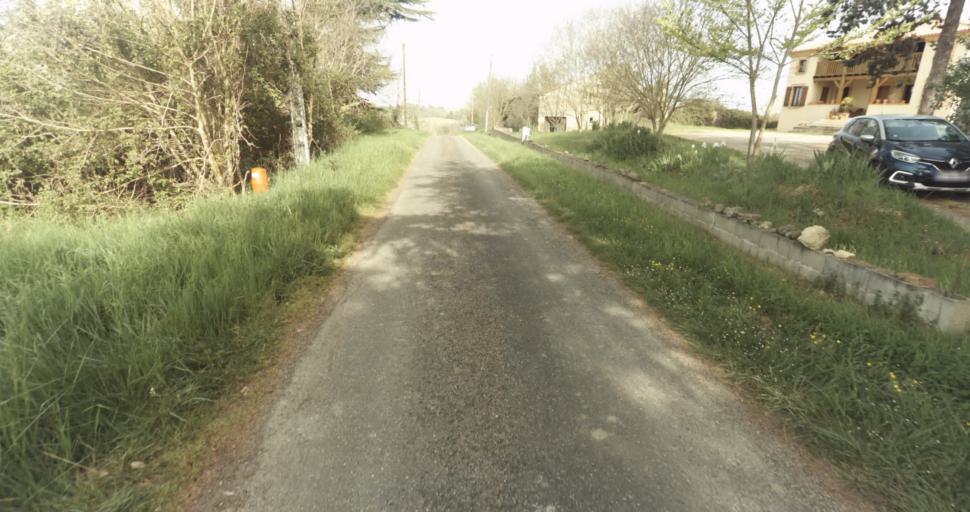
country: FR
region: Midi-Pyrenees
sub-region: Departement du Tarn-et-Garonne
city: Moissac
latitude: 44.1659
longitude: 1.0413
